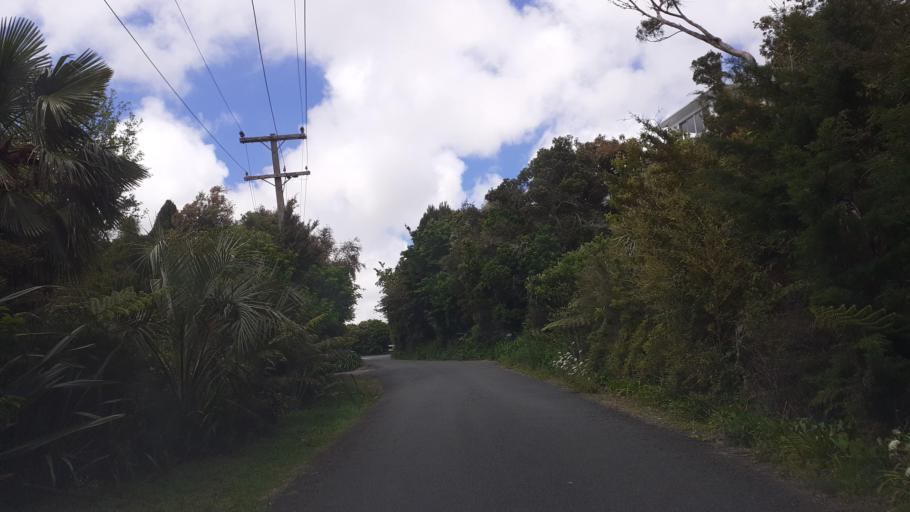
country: NZ
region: Northland
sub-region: Far North District
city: Paihia
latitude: -35.3092
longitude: 174.1128
